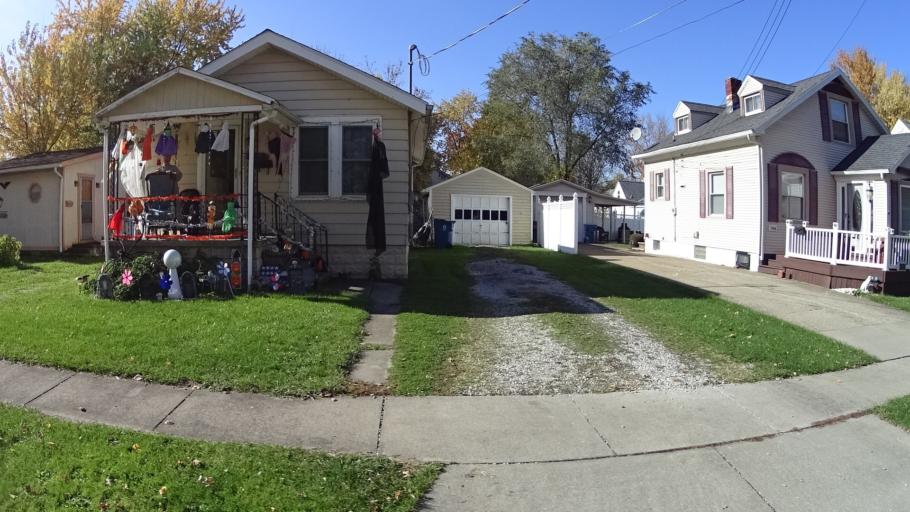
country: US
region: Ohio
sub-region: Lorain County
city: Lorain
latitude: 41.4547
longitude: -82.2043
